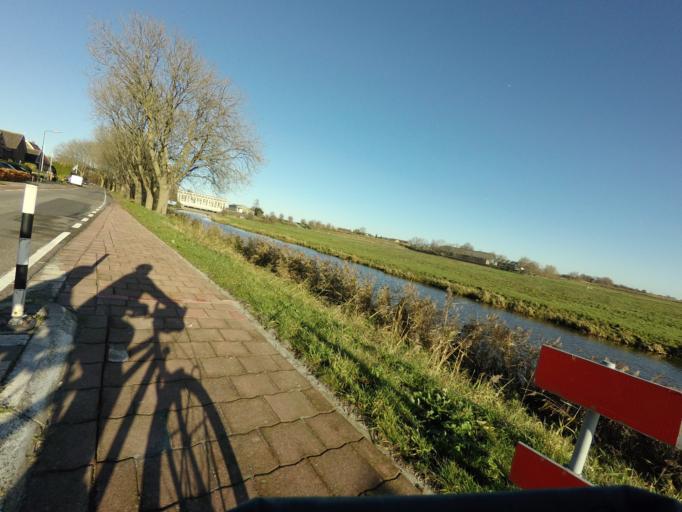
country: NL
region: North Holland
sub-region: Gemeente Ouder-Amstel
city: Ouderkerk aan de Amstel
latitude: 52.2508
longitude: 4.9035
